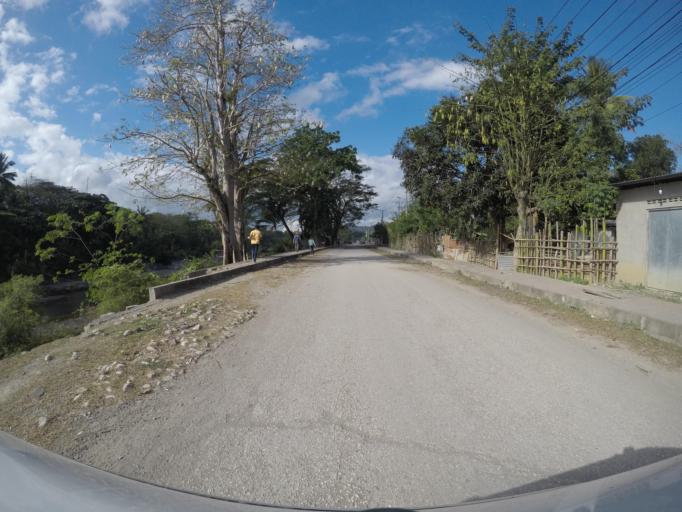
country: TL
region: Viqueque
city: Viqueque
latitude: -8.8569
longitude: 126.3658
